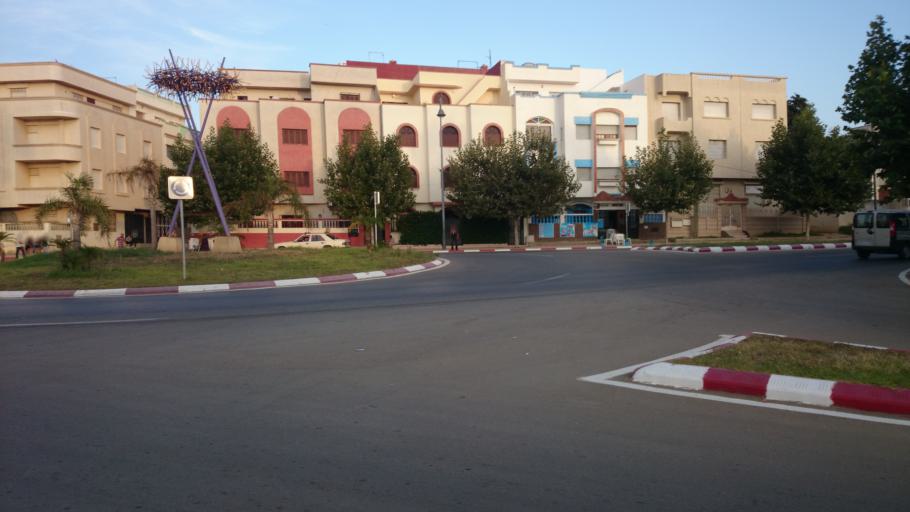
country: MA
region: Tanger-Tetouan
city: Asilah
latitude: 35.4693
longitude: -6.0305
